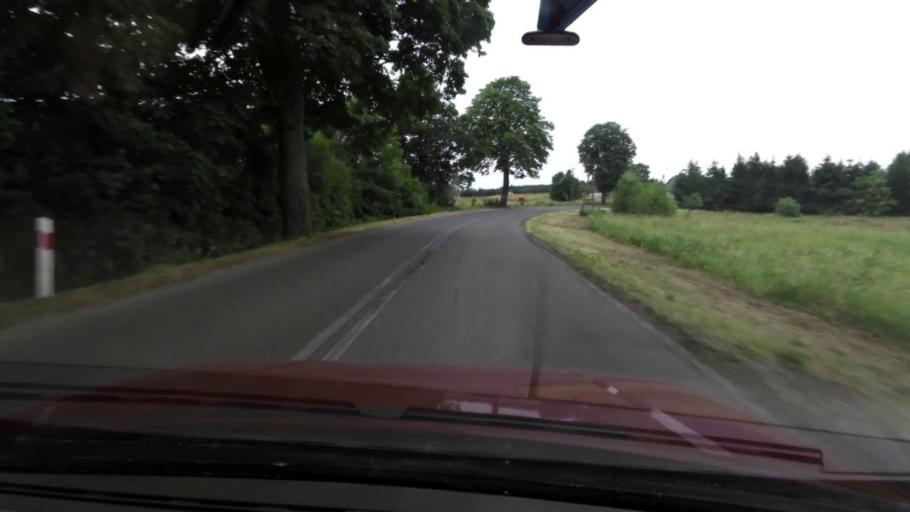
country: PL
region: West Pomeranian Voivodeship
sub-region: Powiat koszalinski
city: Sianow
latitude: 54.1776
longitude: 16.3852
